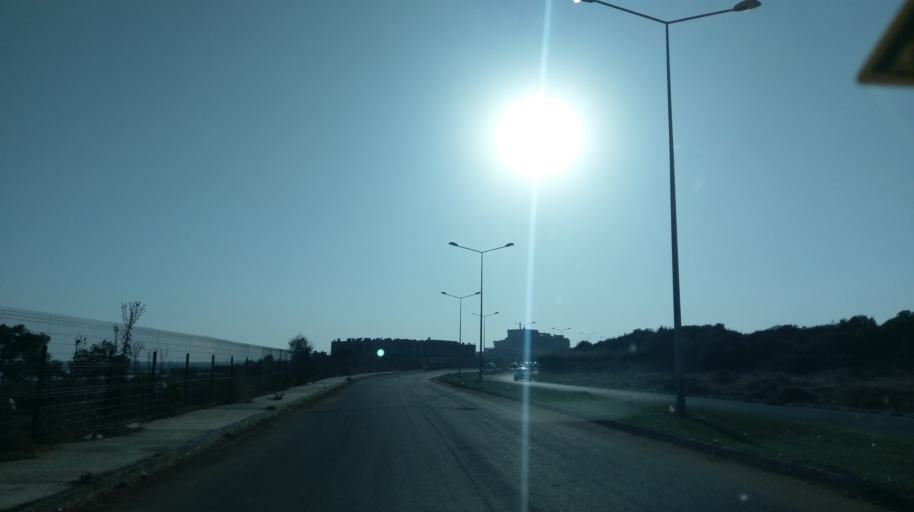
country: CY
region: Ammochostos
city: Leonarisso
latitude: 35.3840
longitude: 34.0956
